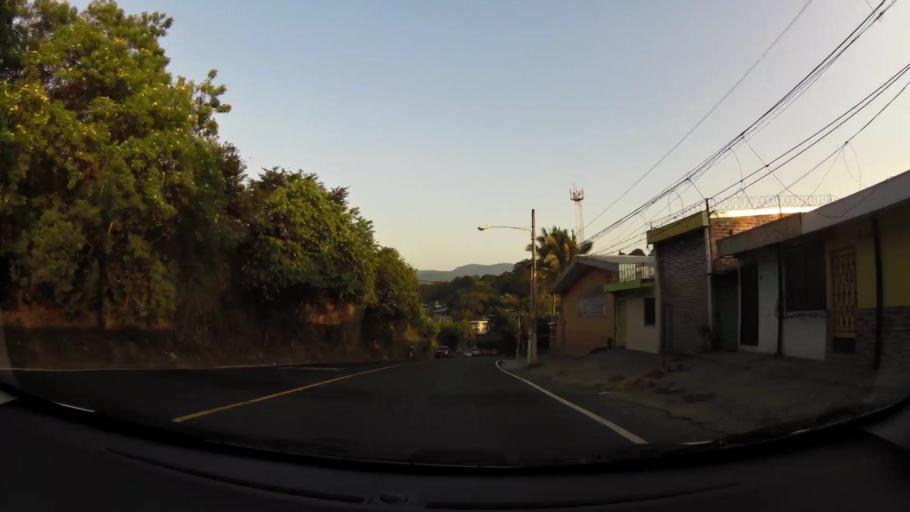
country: SV
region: San Salvador
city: San Salvador
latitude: 13.6861
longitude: -89.2095
